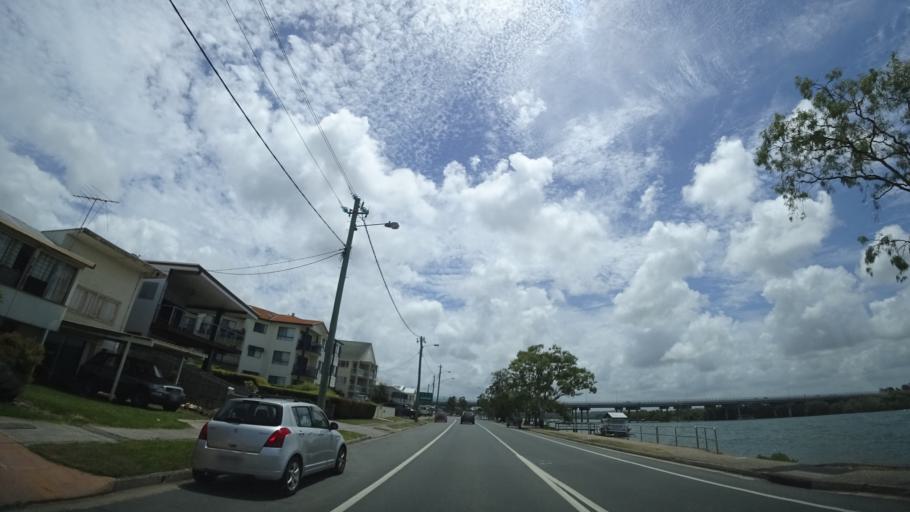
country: AU
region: Queensland
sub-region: Sunshine Coast
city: Buderim
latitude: -26.6421
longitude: 153.0709
